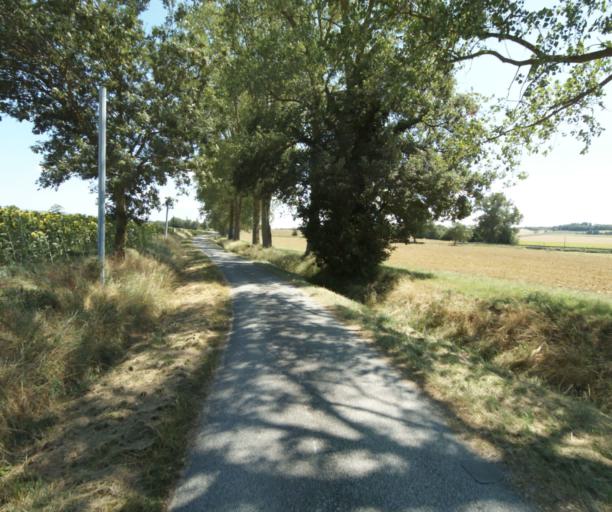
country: FR
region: Midi-Pyrenees
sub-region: Departement de la Haute-Garonne
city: Saint-Felix-Lauragais
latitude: 43.4868
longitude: 1.8785
